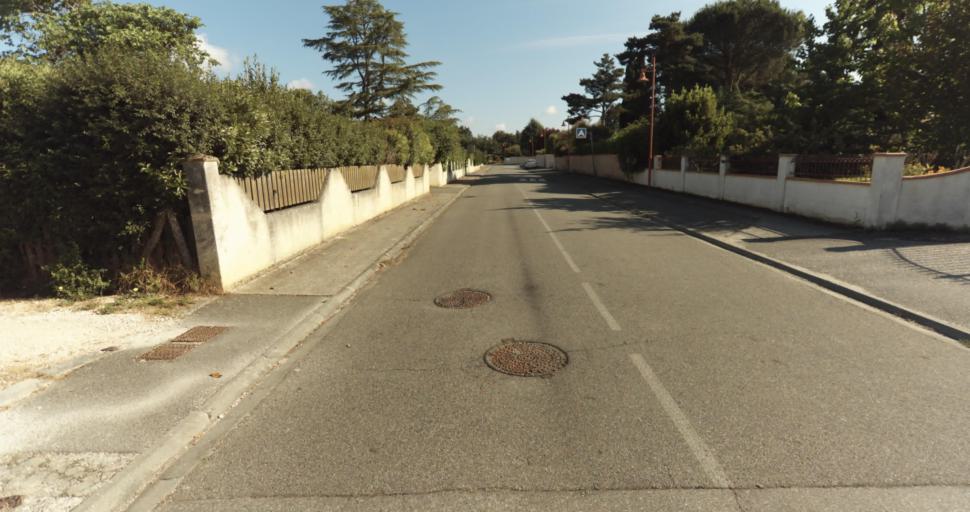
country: FR
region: Midi-Pyrenees
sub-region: Departement de la Haute-Garonne
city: Fontenilles
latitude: 43.5647
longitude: 1.2060
